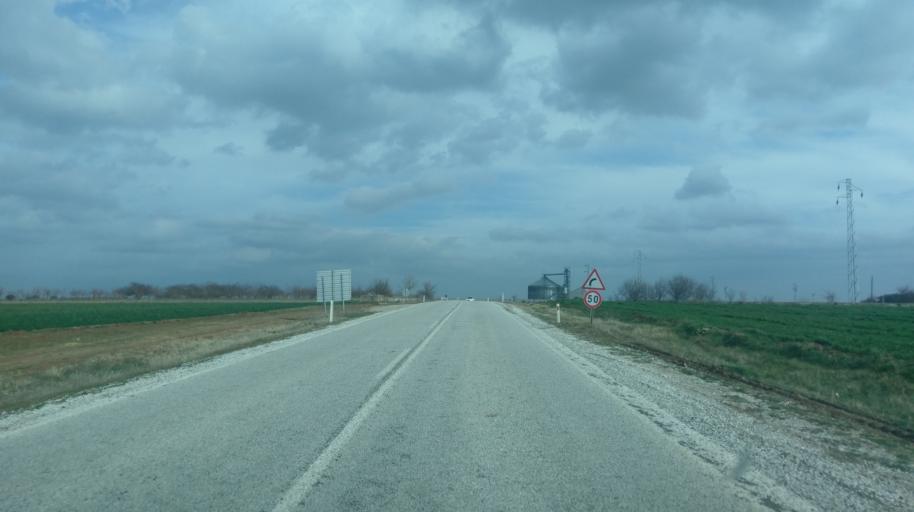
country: TR
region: Kirklareli
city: Inece
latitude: 41.6799
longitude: 27.0535
